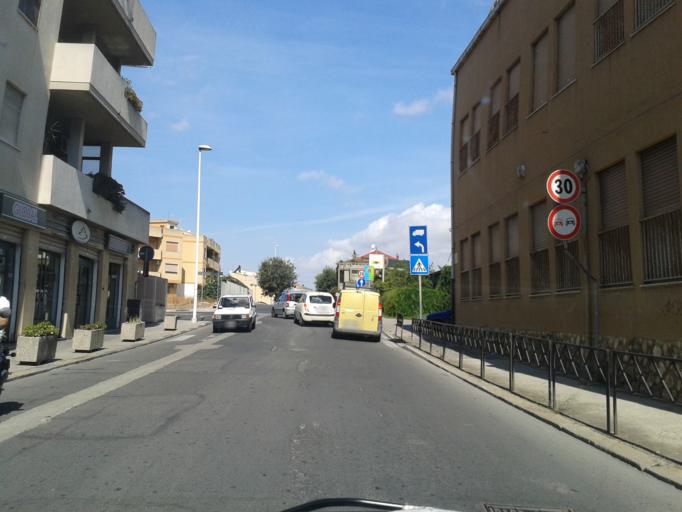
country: IT
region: Sardinia
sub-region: Provincia di Cagliari
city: Quartucciu
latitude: 39.2475
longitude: 9.1815
